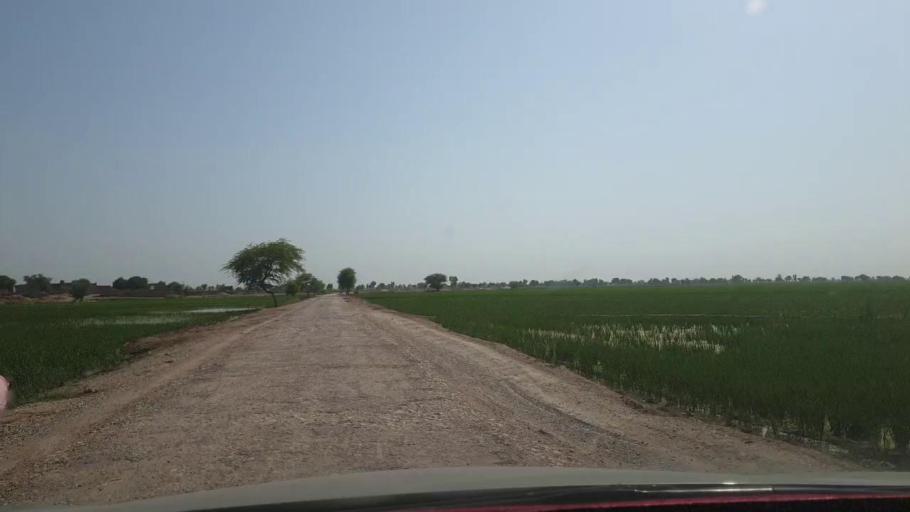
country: PK
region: Sindh
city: Nasirabad
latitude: 27.3603
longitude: 67.8506
